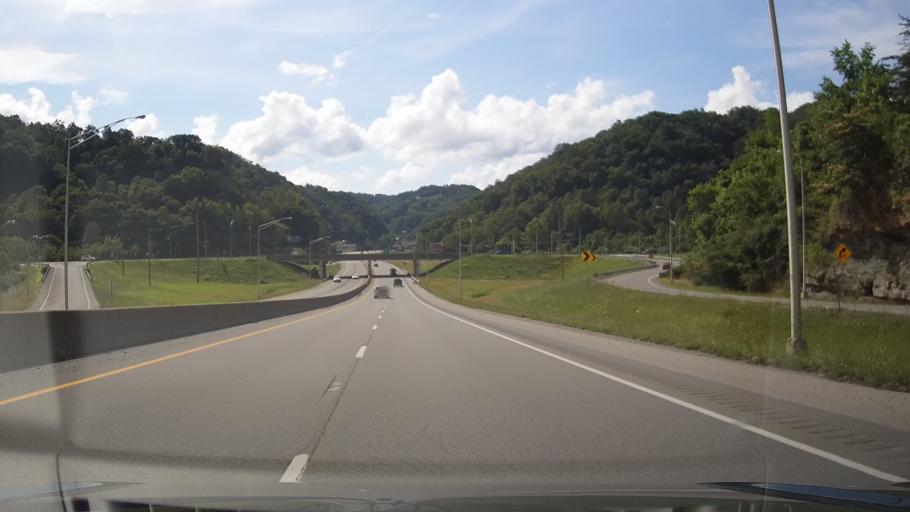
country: US
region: Kentucky
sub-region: Floyd County
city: Prestonsburg
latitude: 37.6349
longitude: -82.7450
